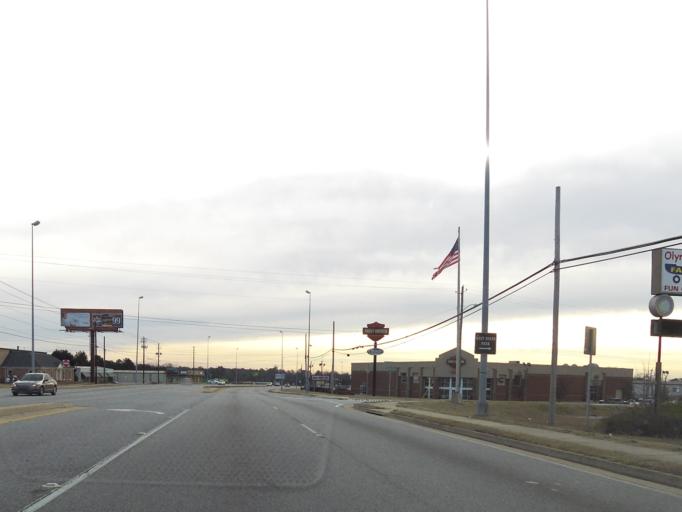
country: US
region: Georgia
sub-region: Bibb County
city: West Point
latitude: 32.8316
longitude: -83.7278
